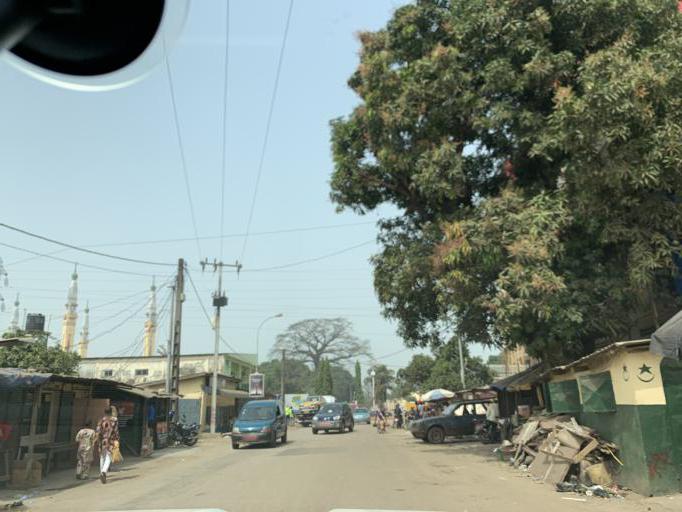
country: GN
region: Conakry
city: Conakry
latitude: 9.5327
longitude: -13.6815
